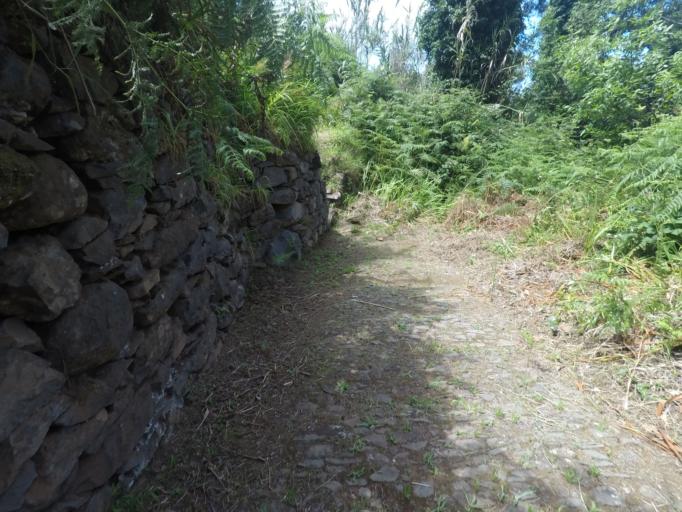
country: PT
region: Madeira
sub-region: Porto Moniz
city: Porto Moniz
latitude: 32.8435
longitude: -17.1501
